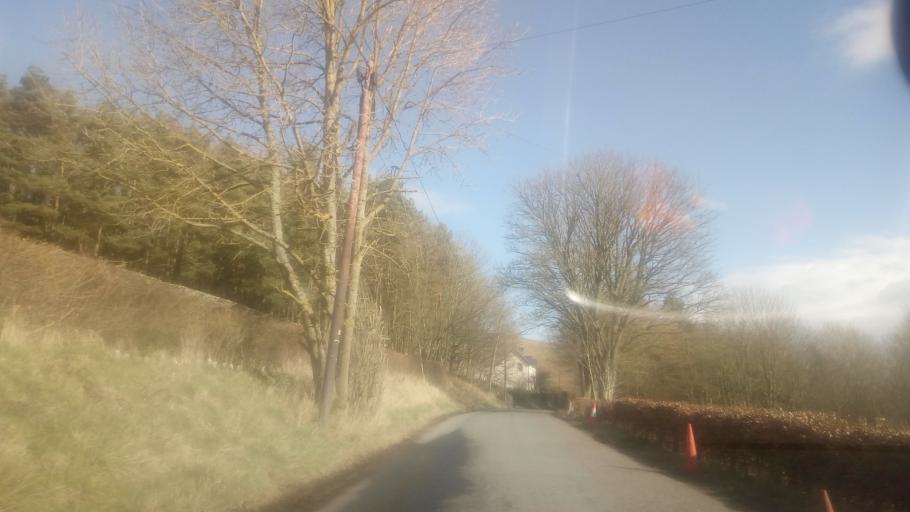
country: GB
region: Scotland
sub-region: The Scottish Borders
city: Hawick
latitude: 55.4175
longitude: -2.8602
